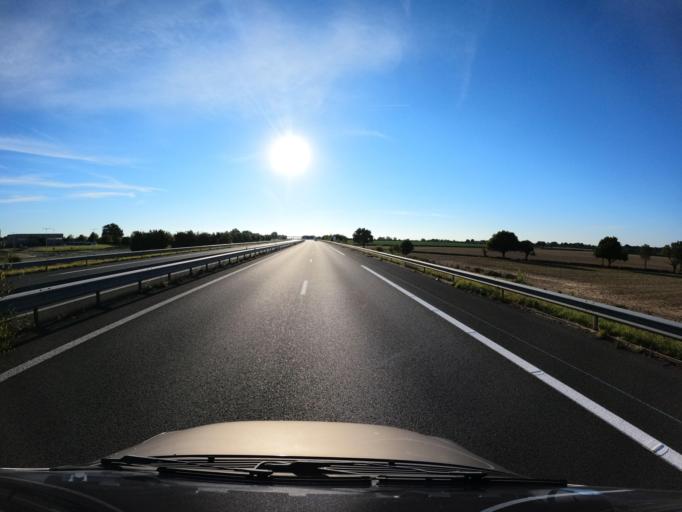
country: FR
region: Pays de la Loire
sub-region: Departement de Maine-et-Loire
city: Chemille-Melay
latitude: 47.2384
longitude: -0.7355
